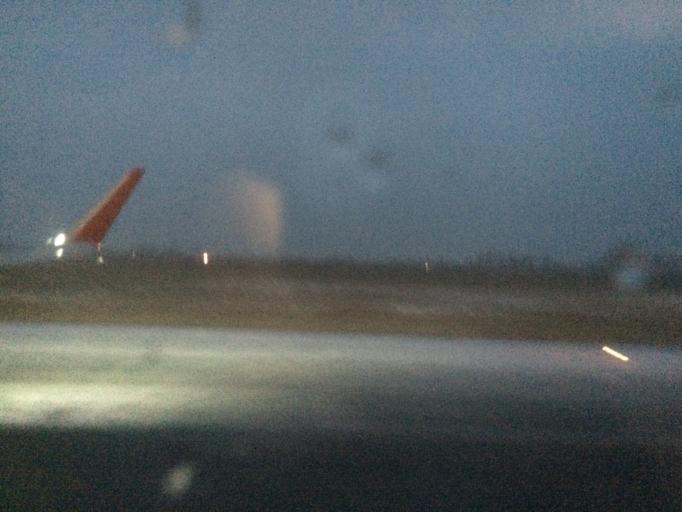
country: RU
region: Novosibirsk
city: Ob'
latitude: 55.0148
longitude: 82.6764
